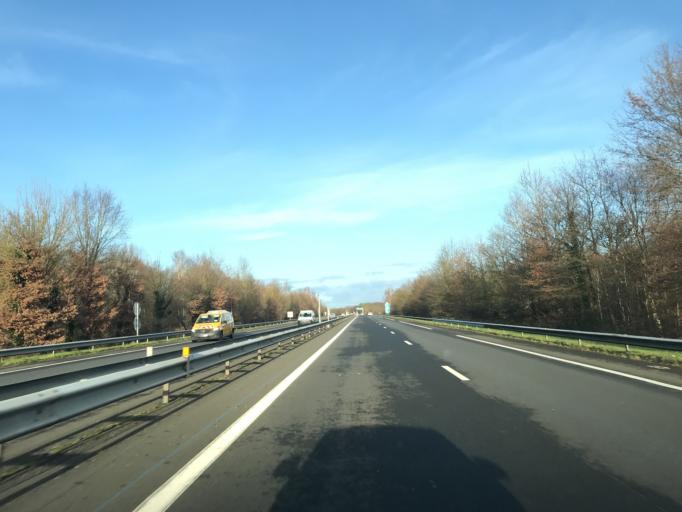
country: FR
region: Pays de la Loire
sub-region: Departement de Maine-et-Loire
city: Durtal
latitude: 47.6172
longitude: -0.2889
